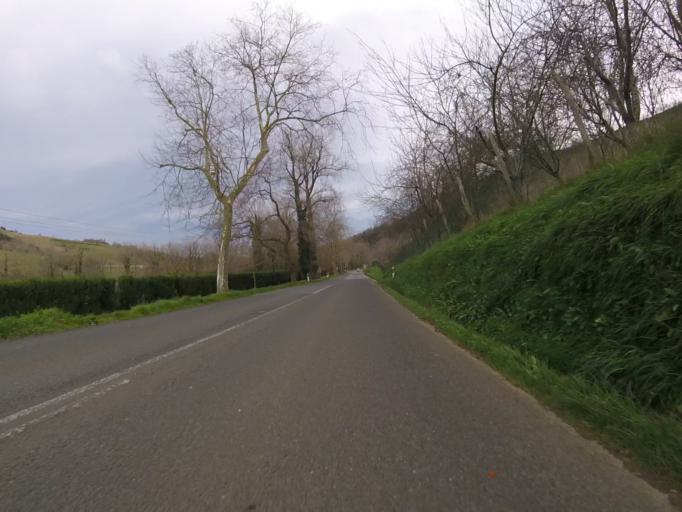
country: ES
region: Basque Country
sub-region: Provincia de Guipuzcoa
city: Aizarnazabal
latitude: 43.2647
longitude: -2.2363
